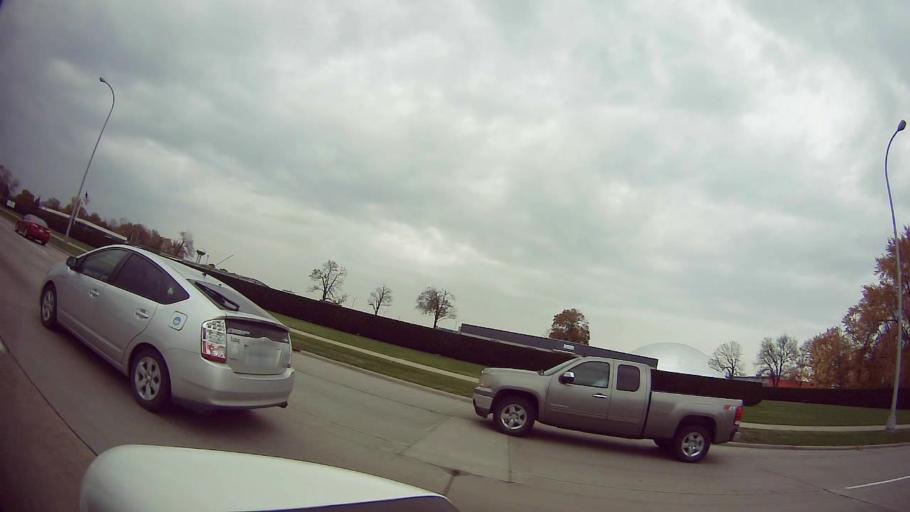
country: US
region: Michigan
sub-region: Macomb County
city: Center Line
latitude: 42.5105
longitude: -83.0465
